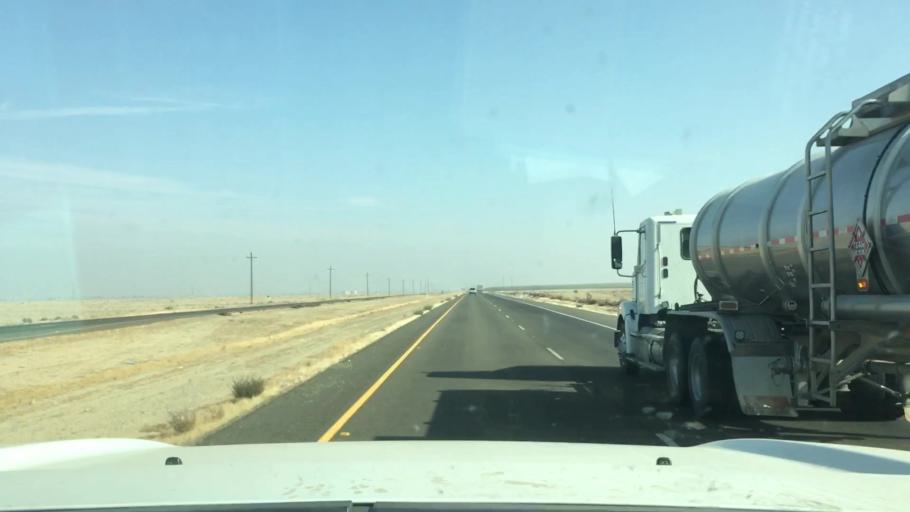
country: US
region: California
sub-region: Kern County
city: Lost Hills
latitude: 35.6157
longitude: -119.7738
